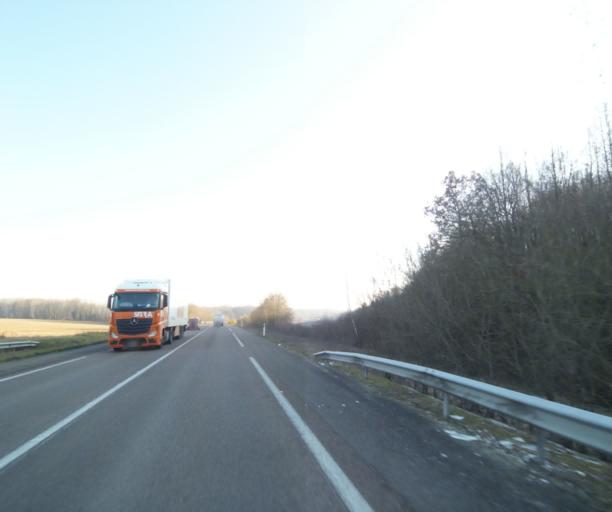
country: FR
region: Champagne-Ardenne
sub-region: Departement de la Haute-Marne
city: Chevillon
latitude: 48.5014
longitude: 5.1054
